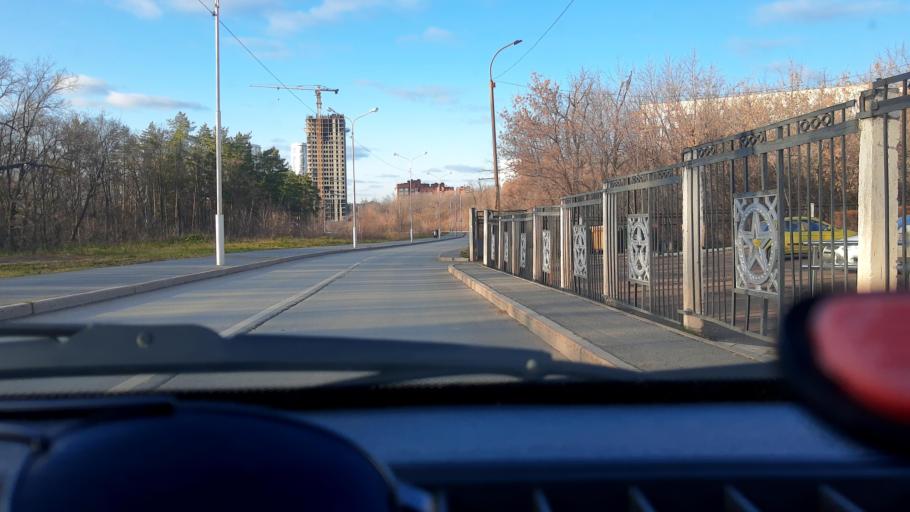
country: RU
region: Bashkortostan
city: Ufa
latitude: 54.7783
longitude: 56.0194
